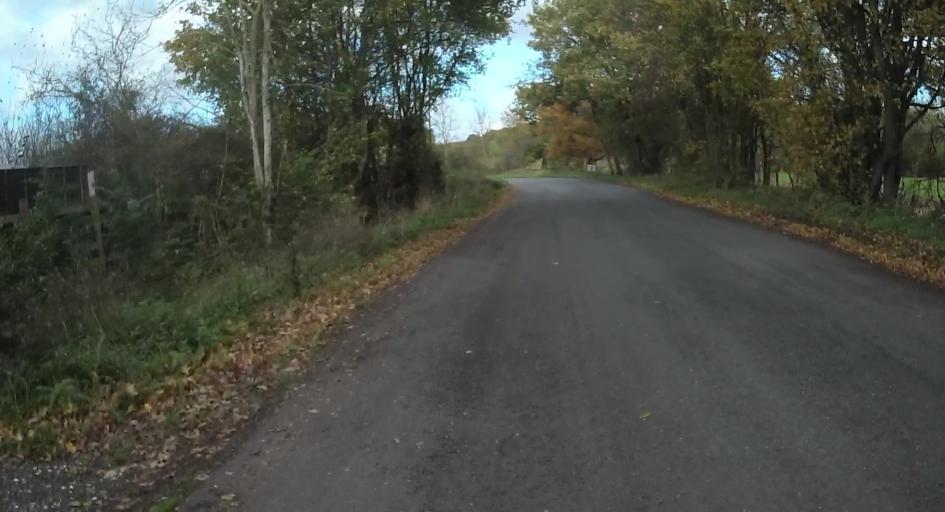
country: GB
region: England
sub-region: Hampshire
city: Basingstoke
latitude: 51.3202
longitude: -1.0720
